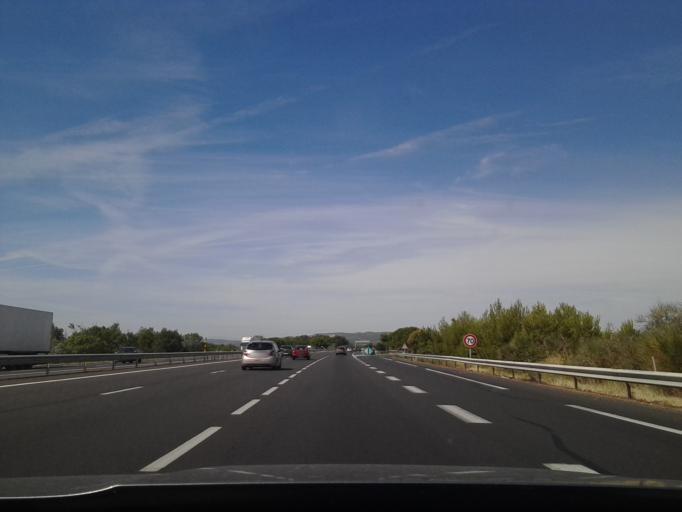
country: FR
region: Languedoc-Roussillon
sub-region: Departement de l'Aude
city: Narbonne
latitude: 43.1776
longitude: 3.0369
